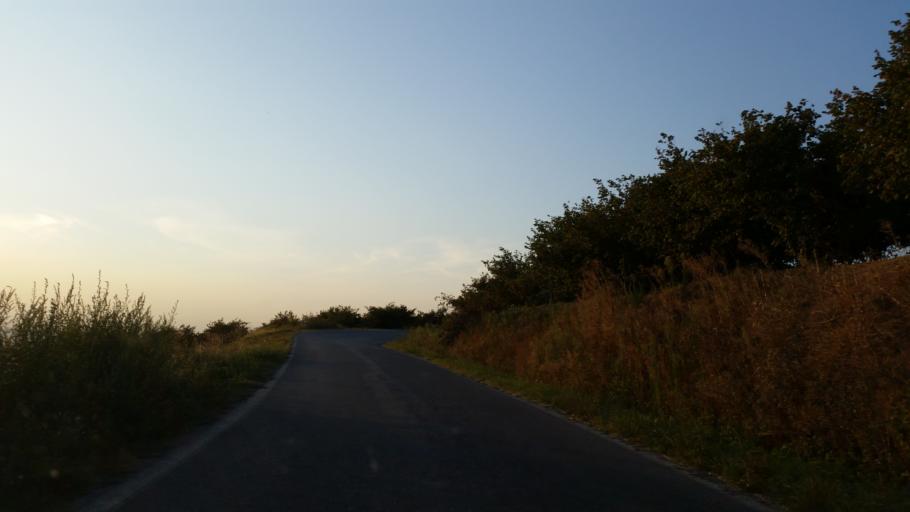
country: IT
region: Piedmont
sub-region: Provincia di Cuneo
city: Trezzo Tinella
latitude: 44.6613
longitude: 8.1334
